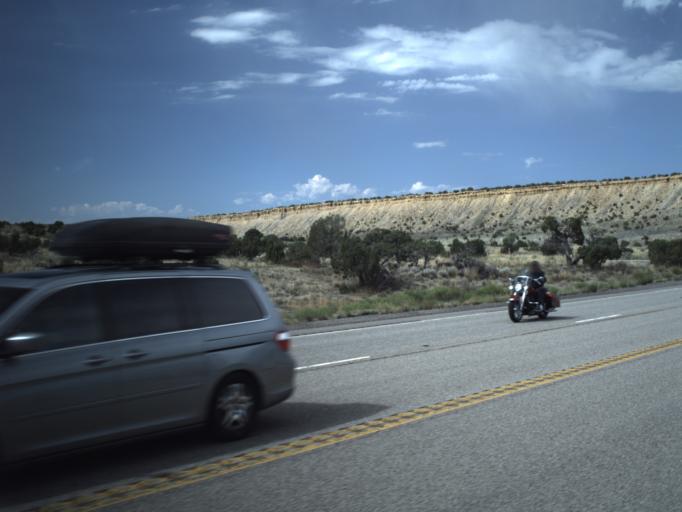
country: US
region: Utah
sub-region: Carbon County
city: Wellington
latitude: 39.5470
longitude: -110.6313
